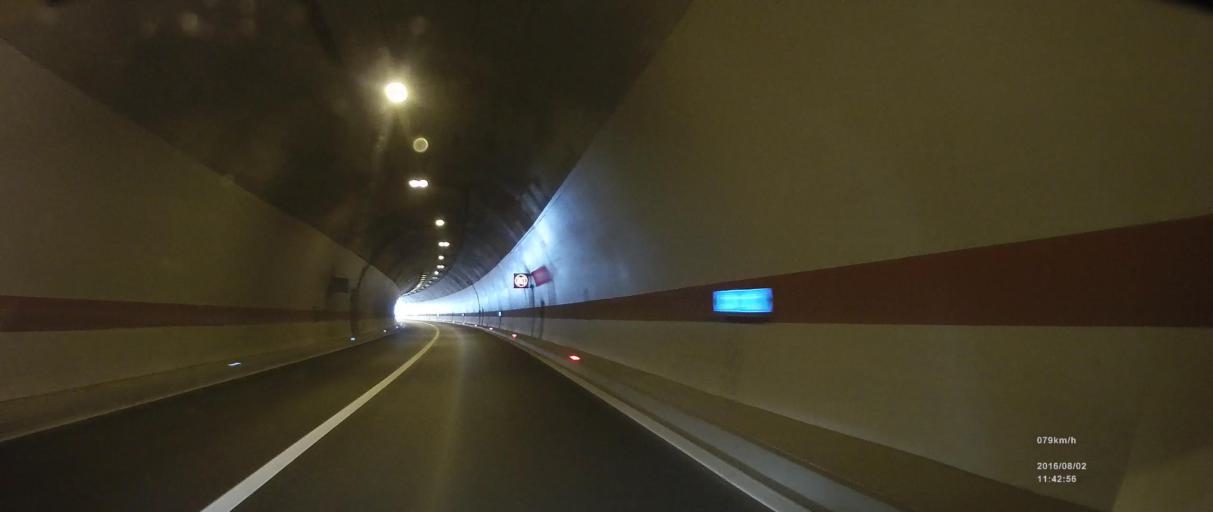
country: HR
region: Dubrovacko-Neretvanska
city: Komin
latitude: 43.0545
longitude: 17.4794
